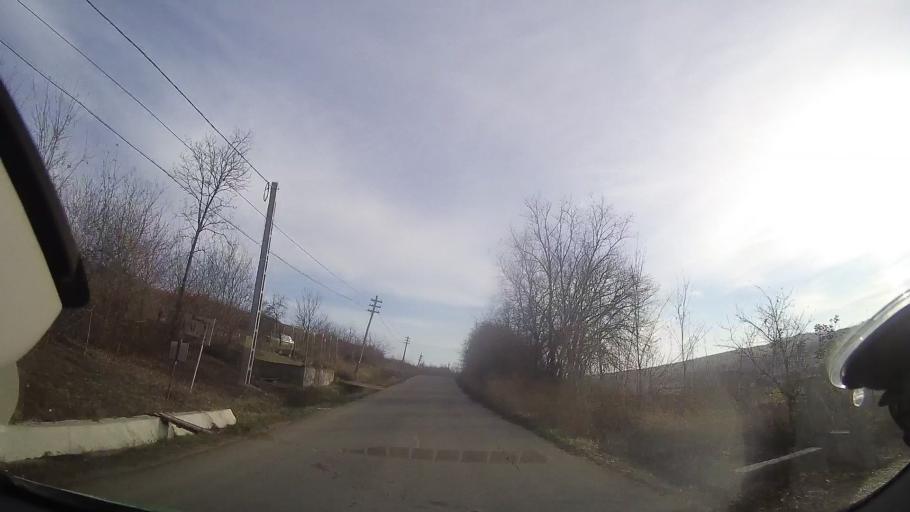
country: RO
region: Bihor
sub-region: Comuna Sarbi
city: Sarbi
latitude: 47.1887
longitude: 22.1259
